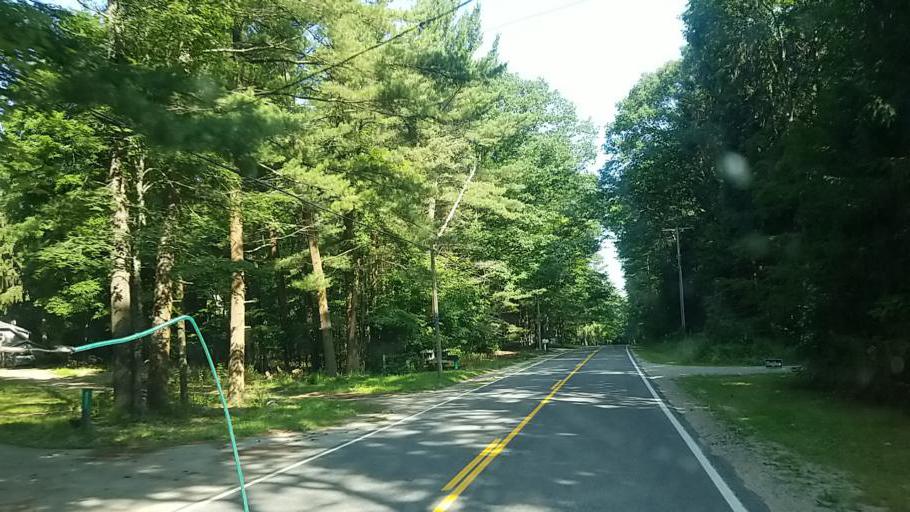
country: US
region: Michigan
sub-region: Muskegon County
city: Whitehall
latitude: 43.3173
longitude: -86.3934
